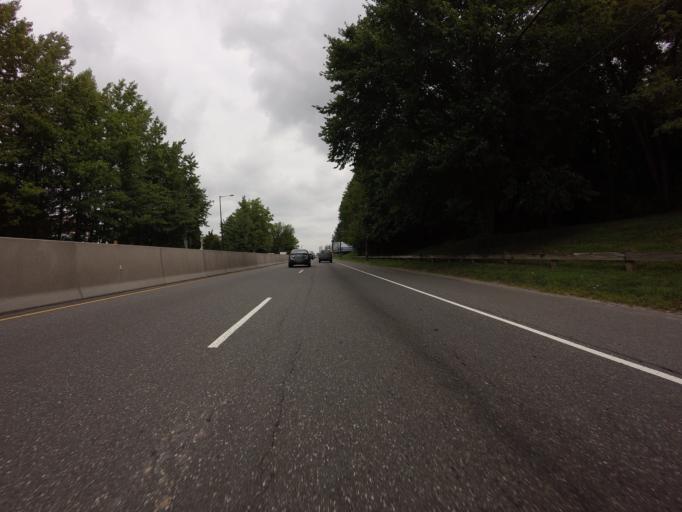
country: US
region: New Jersey
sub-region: Gloucester County
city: National Park
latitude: 39.9079
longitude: -75.1934
